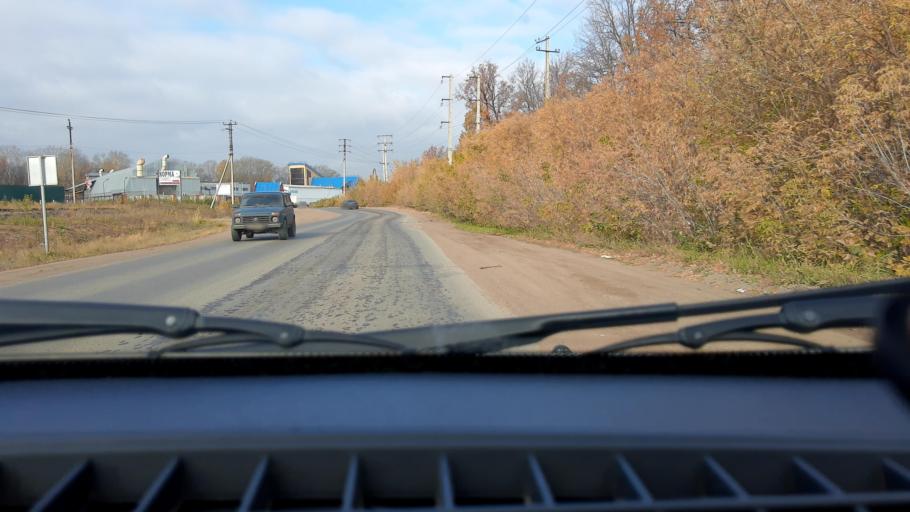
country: RU
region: Bashkortostan
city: Ufa
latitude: 54.5725
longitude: 55.9243
